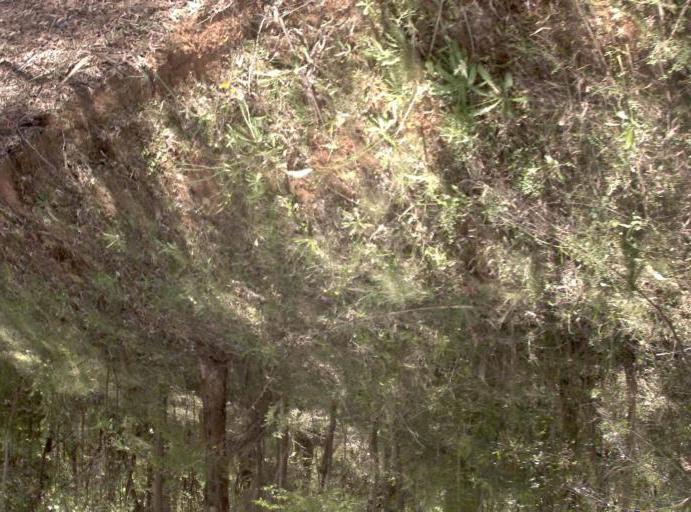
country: AU
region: New South Wales
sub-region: Bombala
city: Bombala
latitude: -37.4750
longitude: 148.9251
